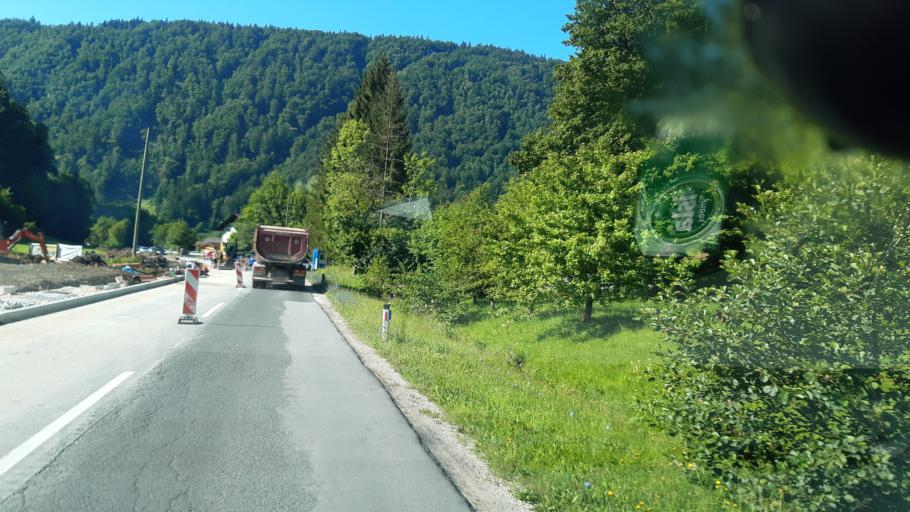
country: SI
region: Kamnik
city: Mekinje
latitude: 46.2305
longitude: 14.6672
